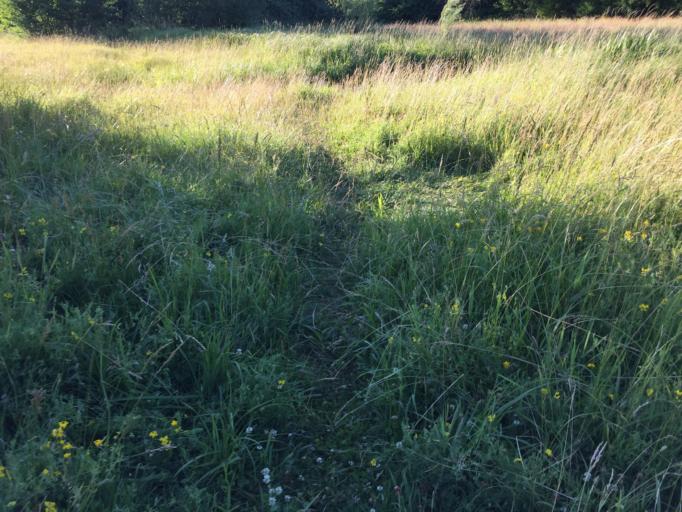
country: DE
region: Bavaria
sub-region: Regierungsbezirk Mittelfranken
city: Erlangen
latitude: 49.5692
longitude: 11.0093
